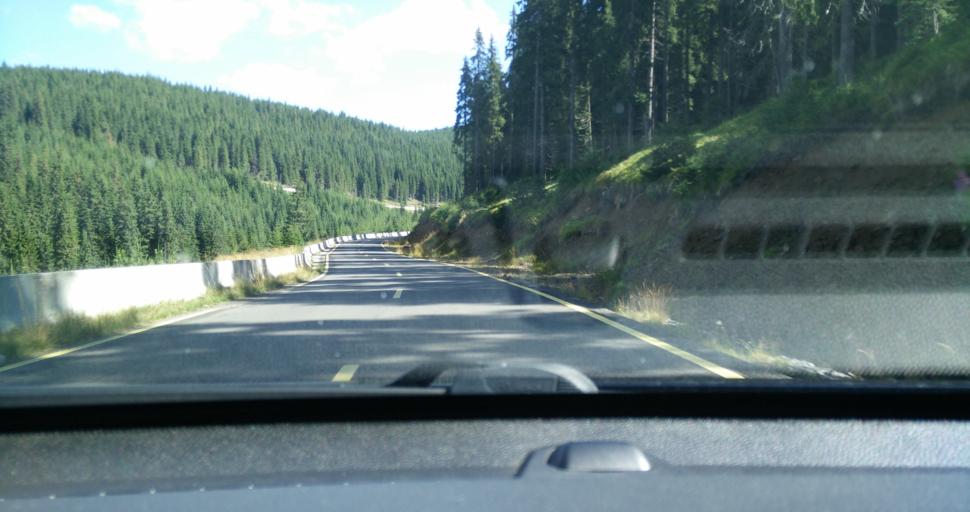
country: RO
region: Hunedoara
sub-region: Oras Petrila
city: Petrila
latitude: 45.4589
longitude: 23.6162
